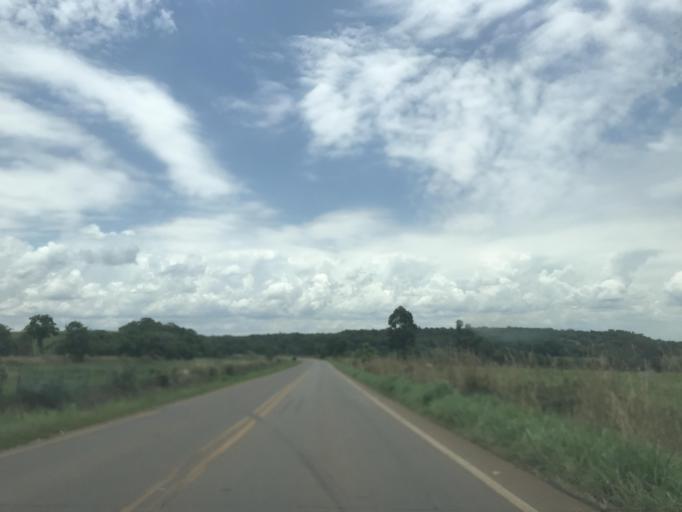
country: BR
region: Goias
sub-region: Vianopolis
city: Vianopolis
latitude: -16.7247
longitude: -48.4252
